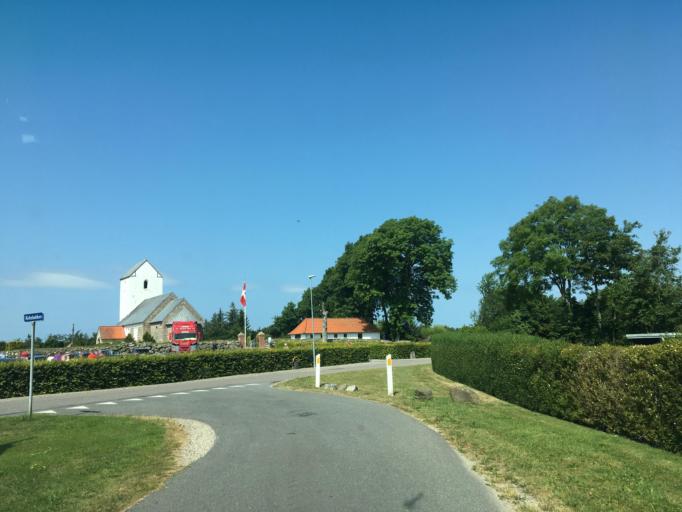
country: DK
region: North Denmark
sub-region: Thisted Kommune
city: Hurup
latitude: 56.8207
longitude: 8.4866
